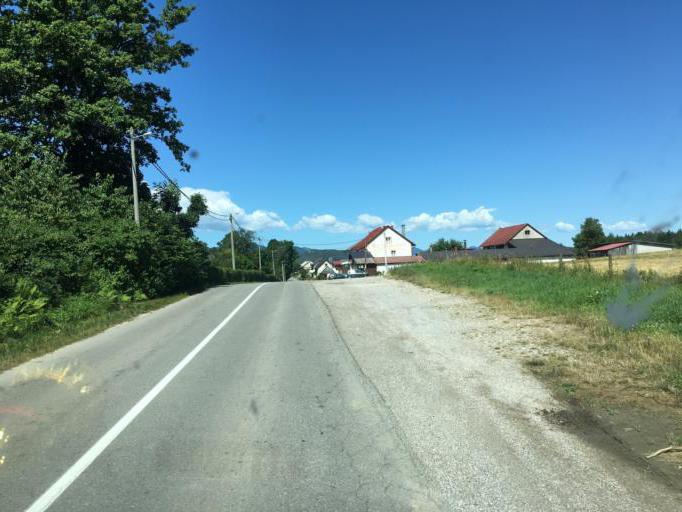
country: HR
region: Licko-Senjska
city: Gospic
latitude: 44.5534
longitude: 15.3523
